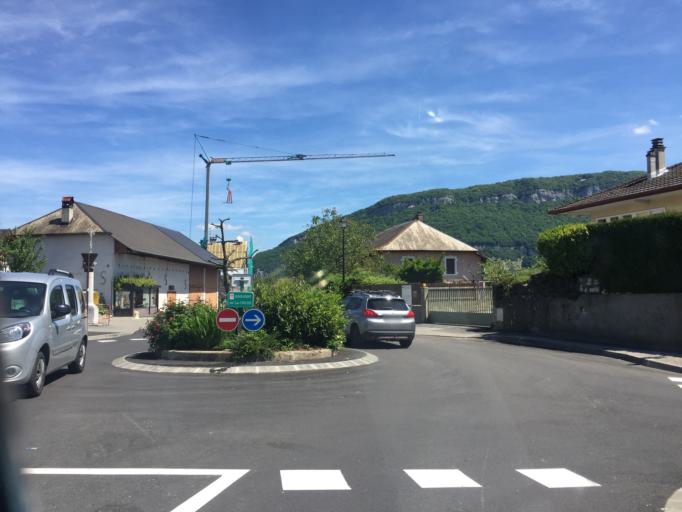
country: FR
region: Rhone-Alpes
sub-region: Departement de la Haute-Savoie
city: Sillingy
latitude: 45.9438
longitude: 6.0329
